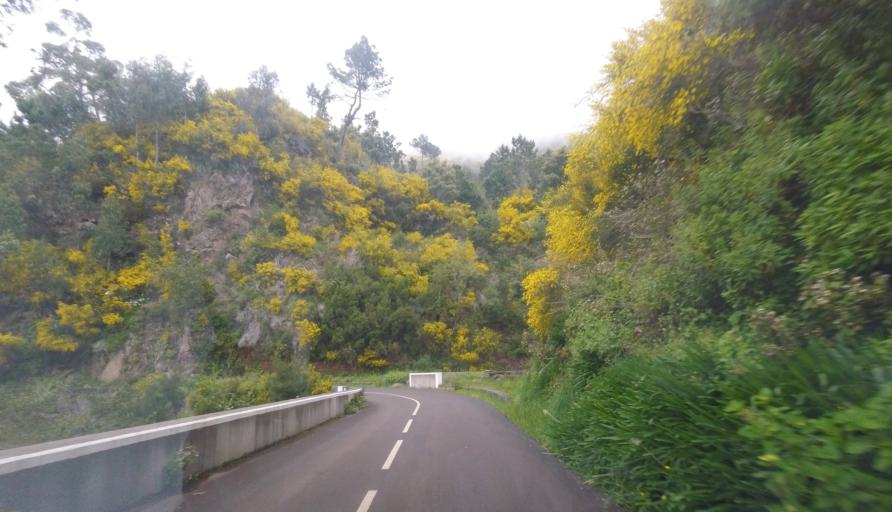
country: PT
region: Madeira
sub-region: Funchal
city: Nossa Senhora do Monte
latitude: 32.6926
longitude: -16.8956
